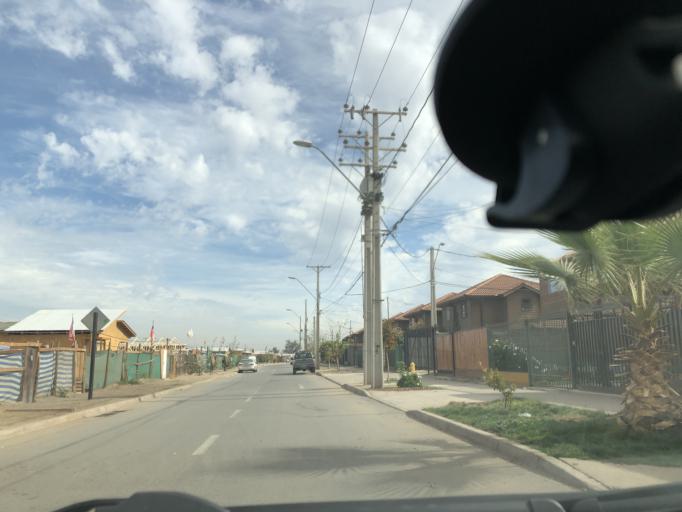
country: CL
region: Santiago Metropolitan
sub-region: Provincia de Cordillera
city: Puente Alto
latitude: -33.6146
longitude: -70.5237
